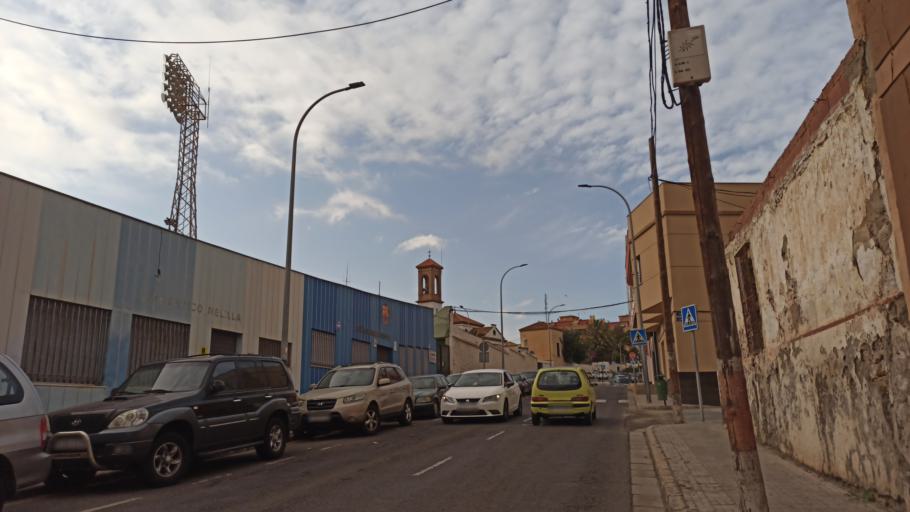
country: ES
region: Melilla
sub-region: Melilla
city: Melilla
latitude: 35.2851
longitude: -2.9481
